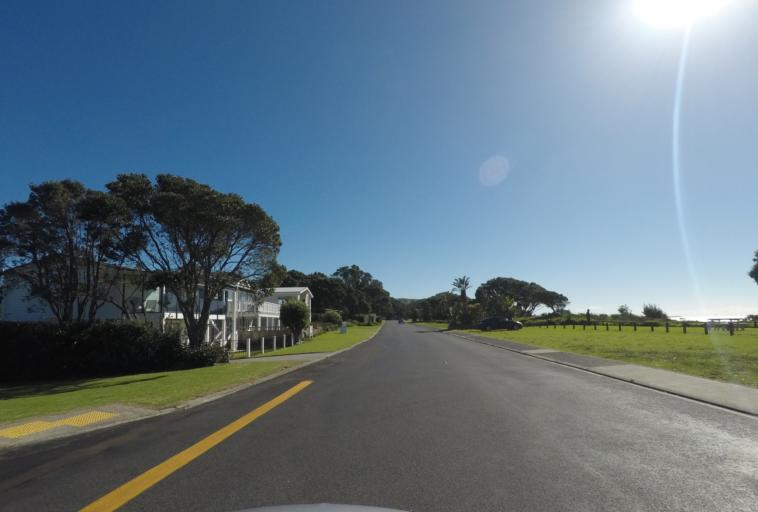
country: NZ
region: Waikato
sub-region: Thames-Coromandel District
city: Whangamata
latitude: -37.2823
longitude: 175.9021
